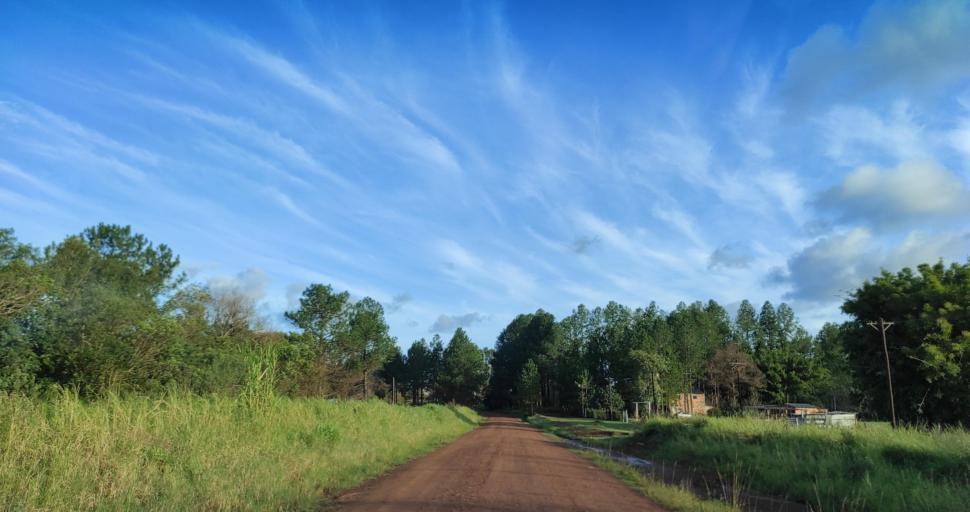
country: AR
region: Misiones
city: Garupa
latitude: -27.5097
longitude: -55.8547
